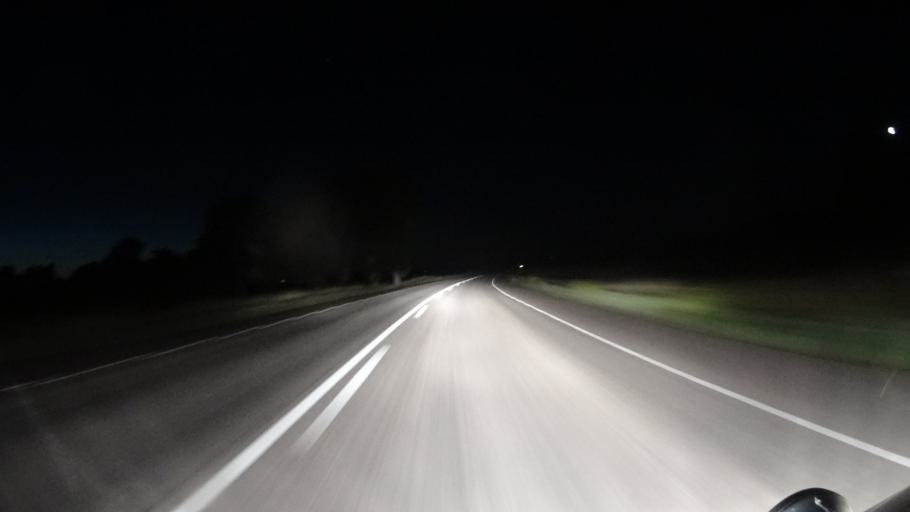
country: SE
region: OEstergoetland
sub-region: Vadstena Kommun
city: Herrestad
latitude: 58.2827
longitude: 14.7616
